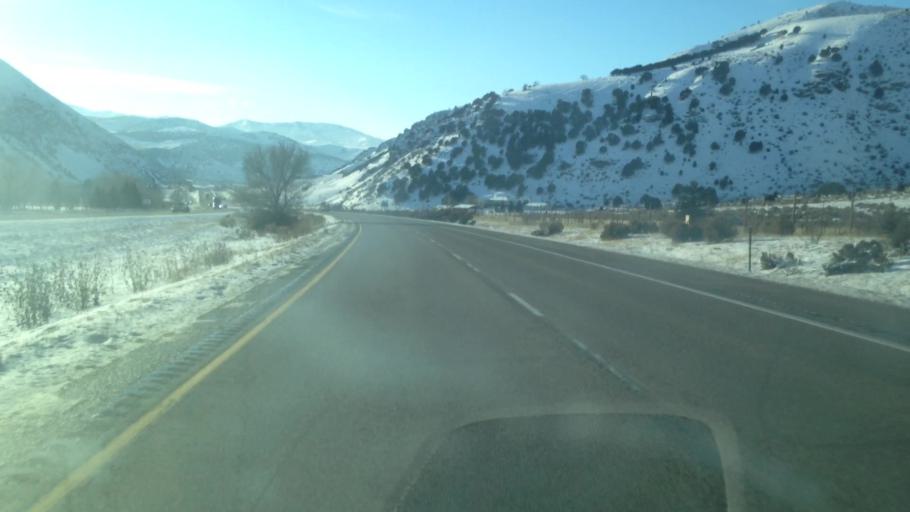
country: US
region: Idaho
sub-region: Bannock County
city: Pocatello
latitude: 42.8018
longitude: -112.3325
